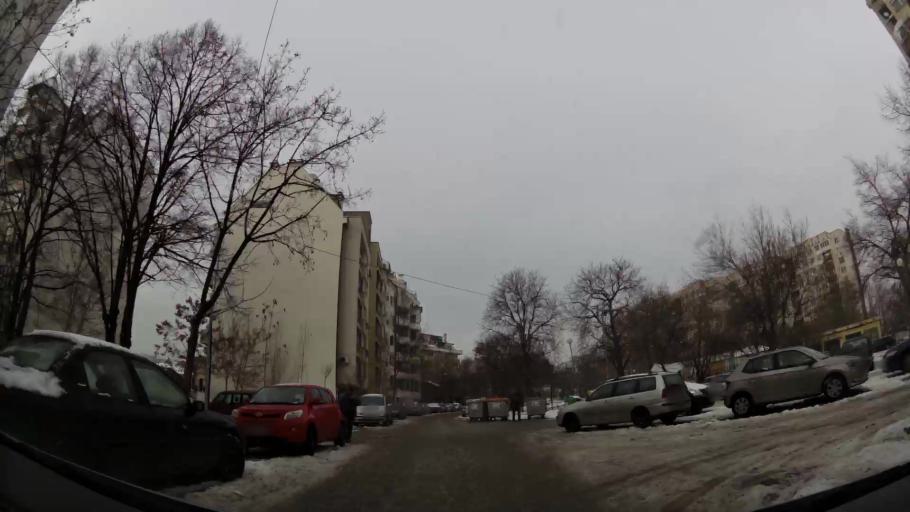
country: BG
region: Sofia-Capital
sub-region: Stolichna Obshtina
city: Sofia
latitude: 42.7086
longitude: 23.3093
